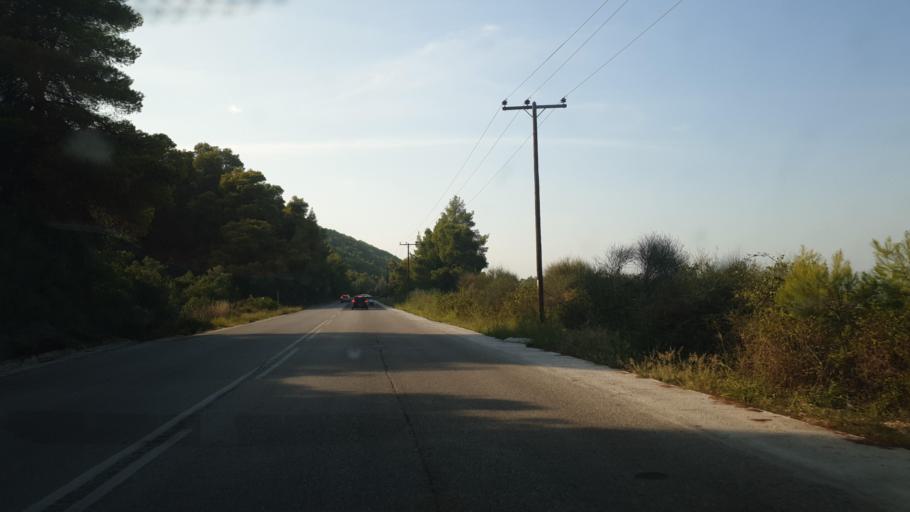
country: GR
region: Central Macedonia
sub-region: Nomos Chalkidikis
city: Agios Nikolaos
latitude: 40.1981
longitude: 23.7668
